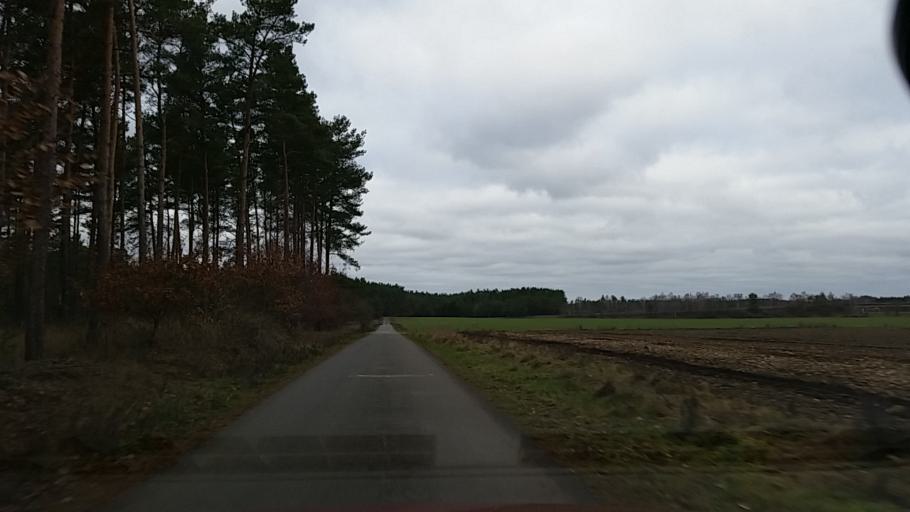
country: DE
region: Lower Saxony
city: Wieren
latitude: 52.8589
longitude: 10.6580
